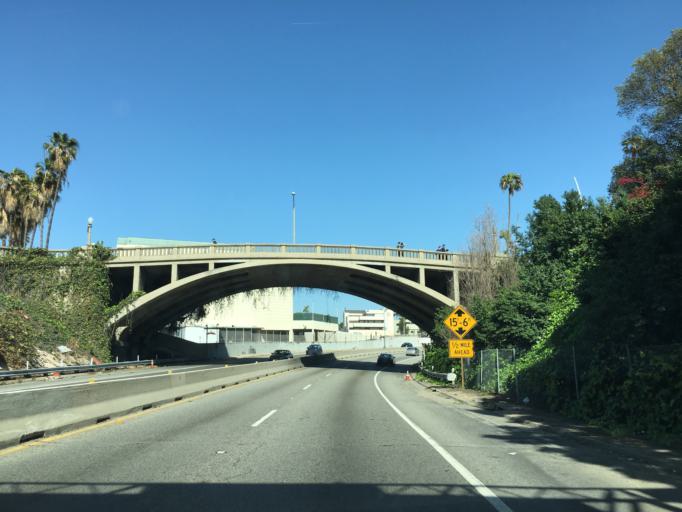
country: US
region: California
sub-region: Los Angeles County
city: Santa Monica
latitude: 34.0118
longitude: -118.4934
